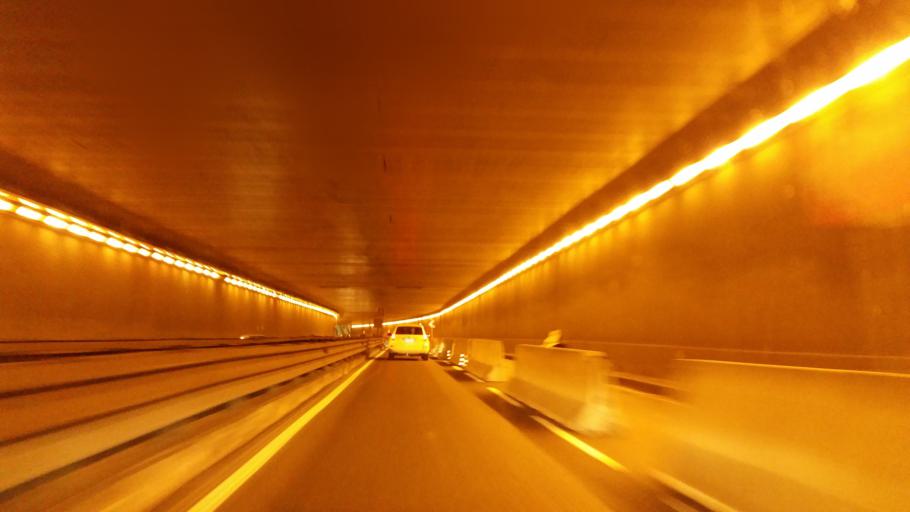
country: IT
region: Piedmont
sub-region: Provincia di Torino
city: Turin
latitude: 45.0444
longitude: 7.6777
